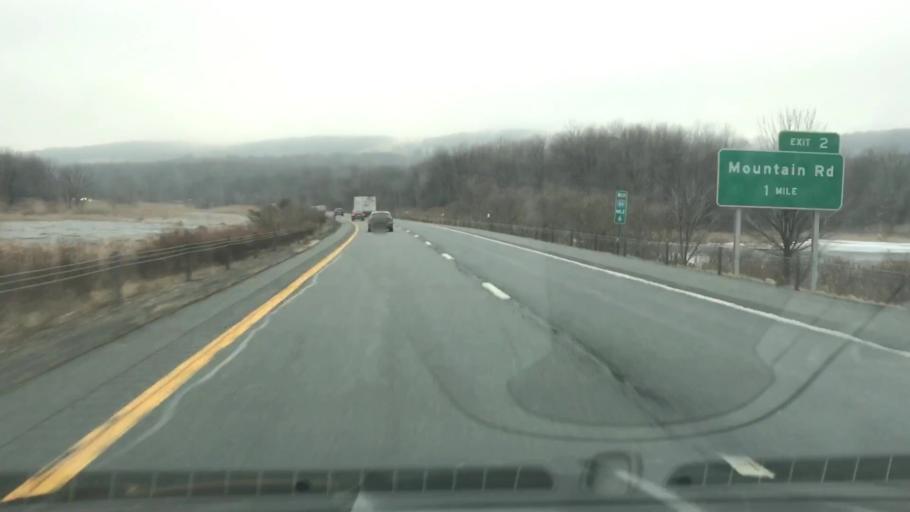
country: US
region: New York
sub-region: Orange County
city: Port Jervis
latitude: 41.3821
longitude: -74.5927
